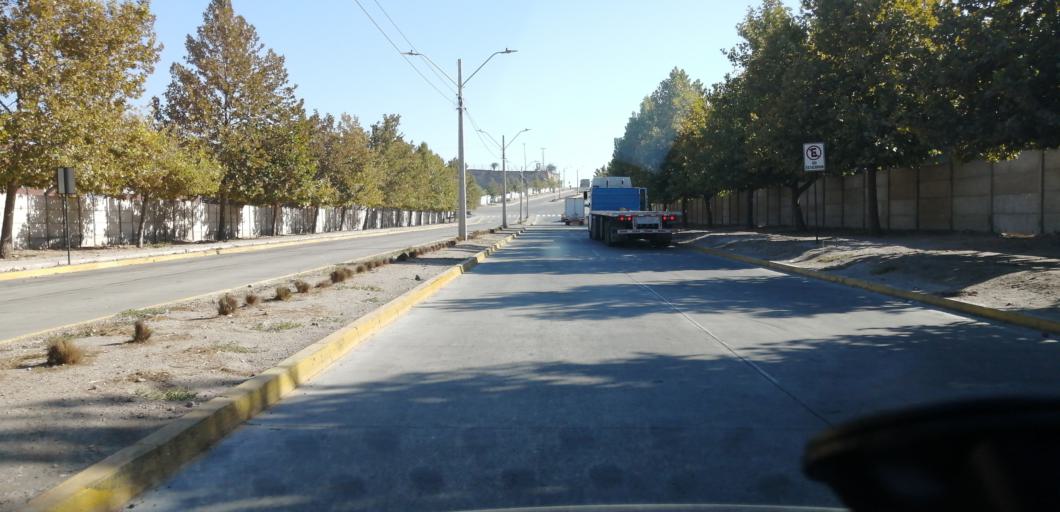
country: CL
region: Santiago Metropolitan
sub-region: Provincia de Santiago
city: Lo Prado
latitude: -33.4556
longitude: -70.7979
